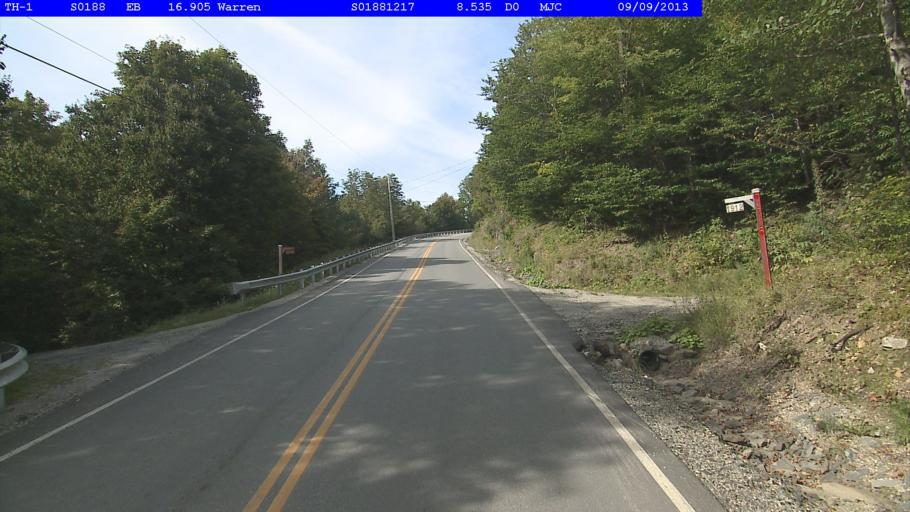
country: US
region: Vermont
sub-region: Washington County
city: Northfield
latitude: 44.1062
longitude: -72.7914
